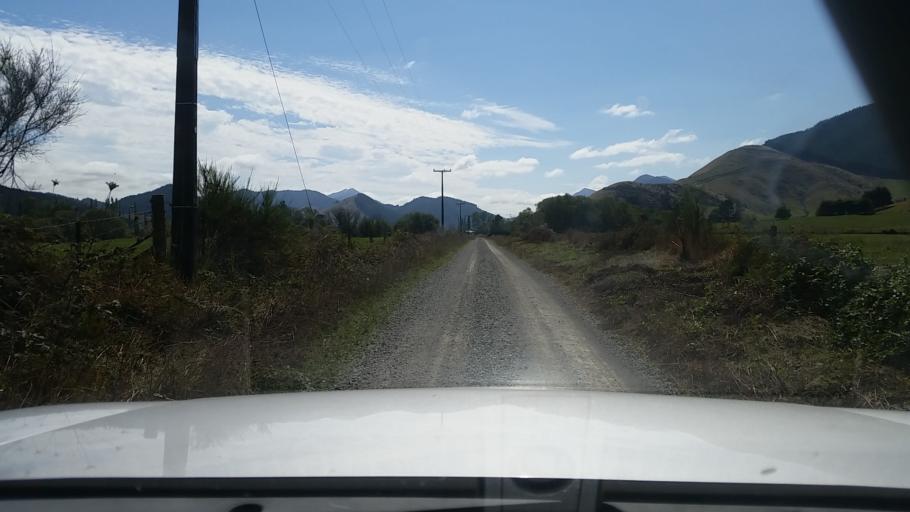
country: NZ
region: Nelson
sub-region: Nelson City
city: Nelson
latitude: -41.2565
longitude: 173.5820
